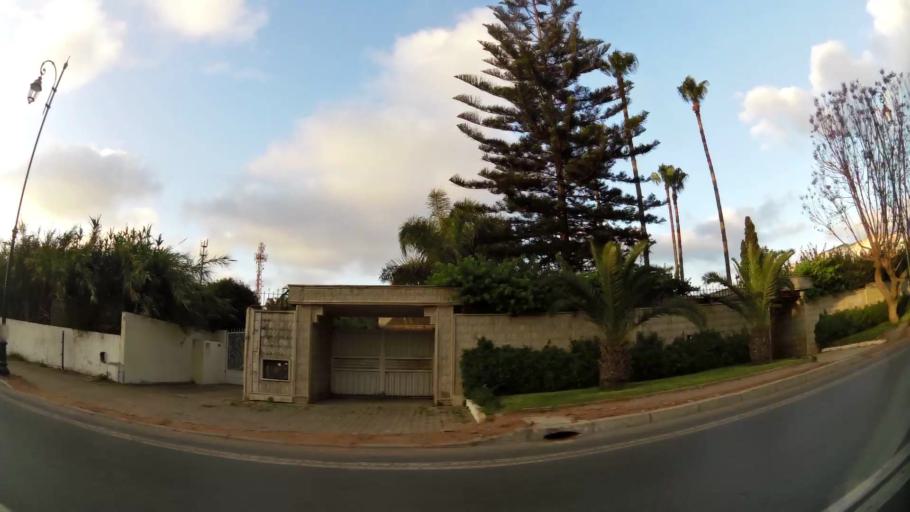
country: MA
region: Rabat-Sale-Zemmour-Zaer
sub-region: Rabat
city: Rabat
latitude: 33.9755
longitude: -6.8368
